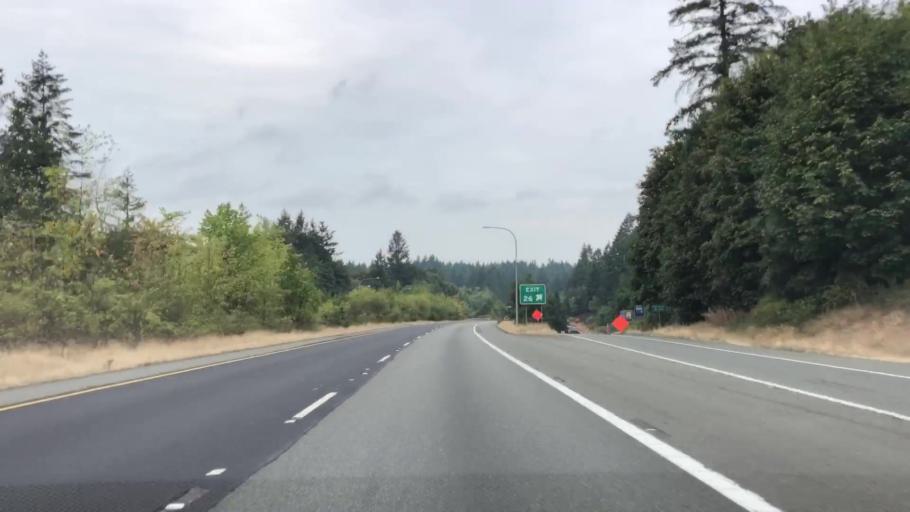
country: US
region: Washington
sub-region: Kitsap County
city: Port Orchard
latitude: 47.5189
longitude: -122.6589
